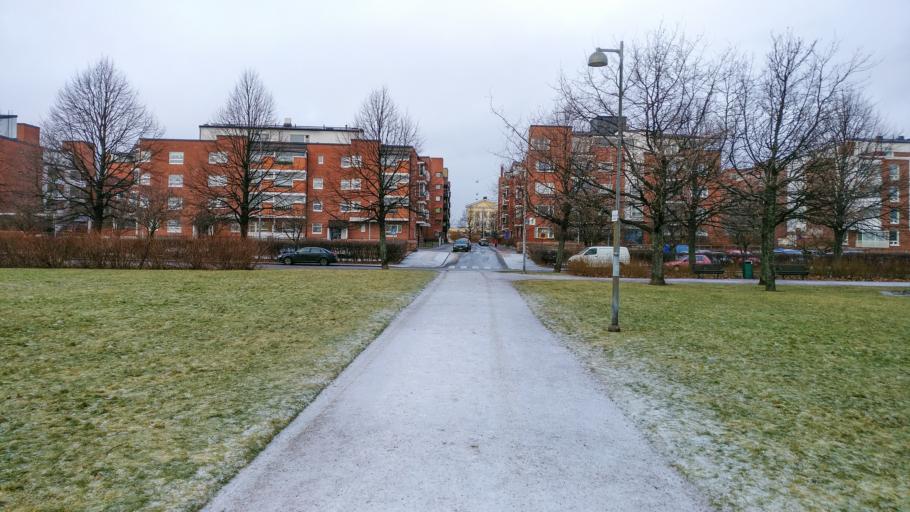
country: FI
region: Uusimaa
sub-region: Helsinki
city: Helsinki
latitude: 60.1658
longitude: 24.9764
